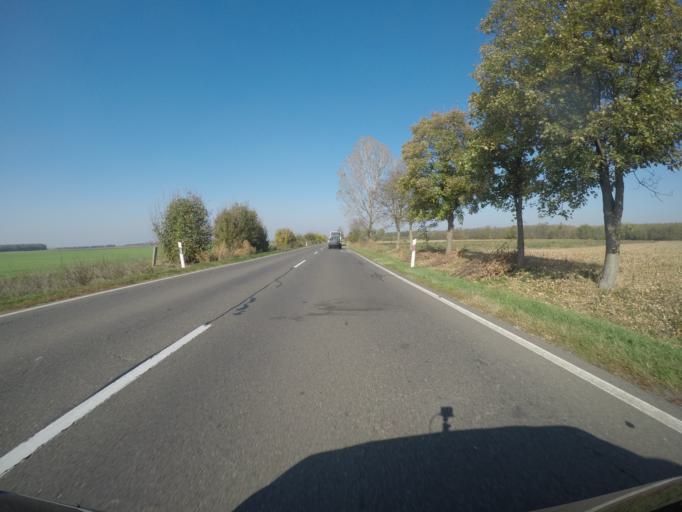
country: HU
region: Tolna
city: Szedres
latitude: 46.5011
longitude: 18.6701
